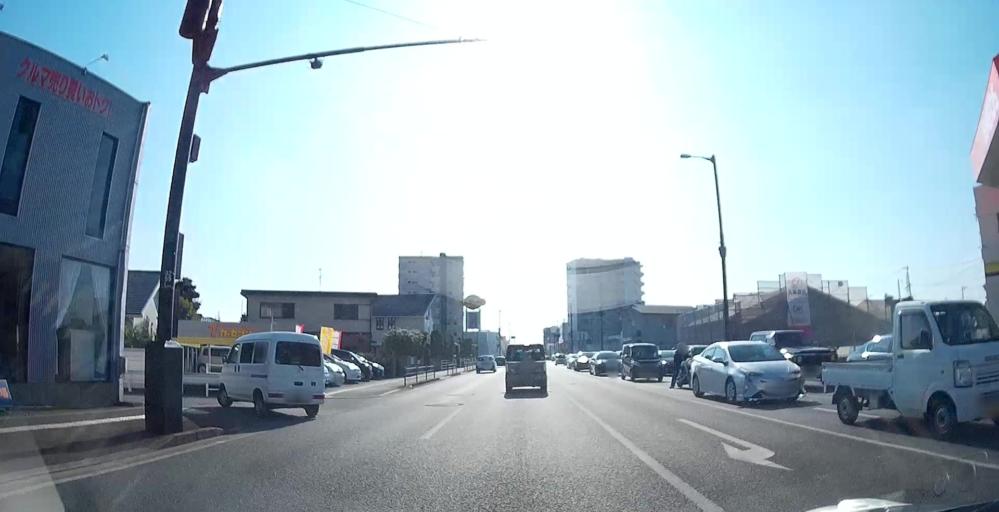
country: JP
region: Kumamoto
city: Kumamoto
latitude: 32.7713
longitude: 130.6939
